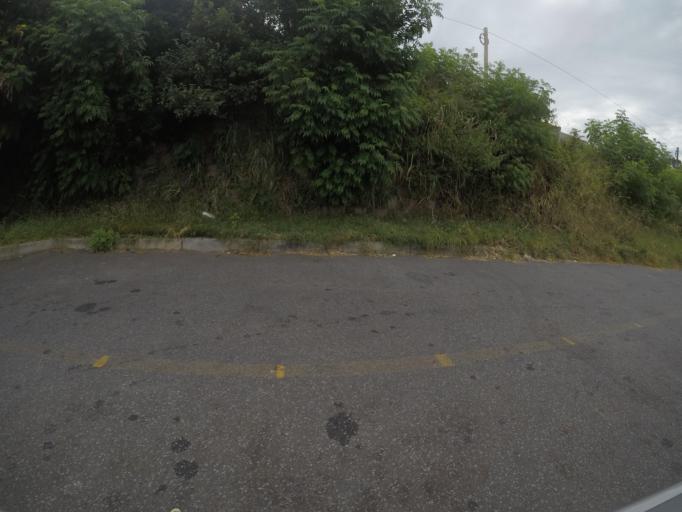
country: ZA
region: Eastern Cape
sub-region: Buffalo City Metropolitan Municipality
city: East London
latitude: -32.9940
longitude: 27.8637
